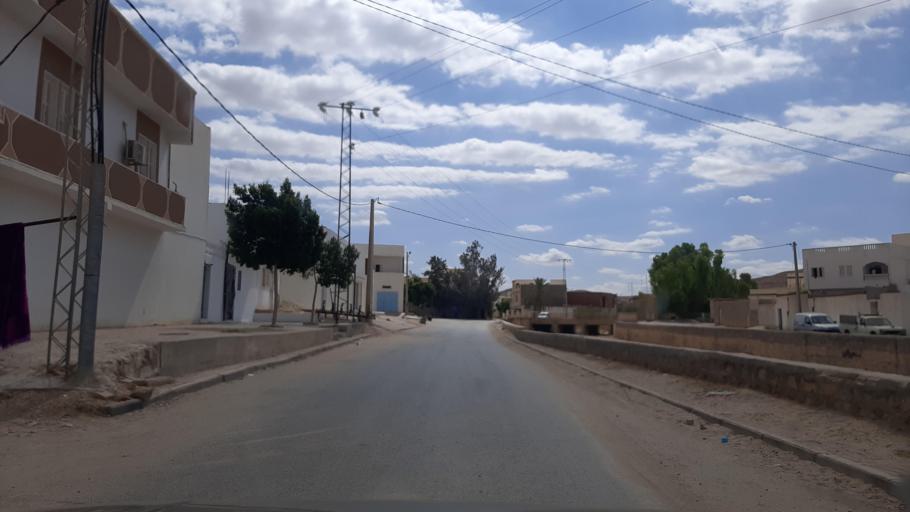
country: TN
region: Tataouine
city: Tataouine
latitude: 32.9293
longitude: 10.4575
